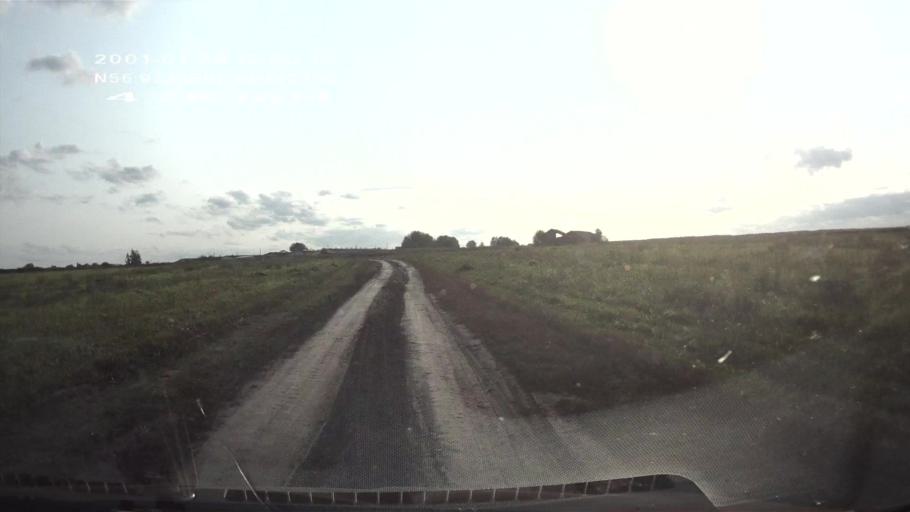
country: RU
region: Mariy-El
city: Kuzhener
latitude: 56.9718
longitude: 48.7913
